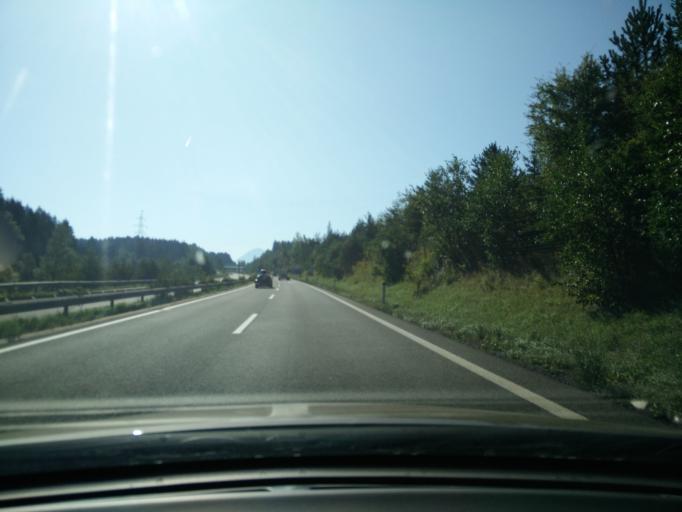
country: AT
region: Carinthia
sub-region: Politischer Bezirk Villach Land
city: Rosegg
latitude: 46.5826
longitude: 13.9908
